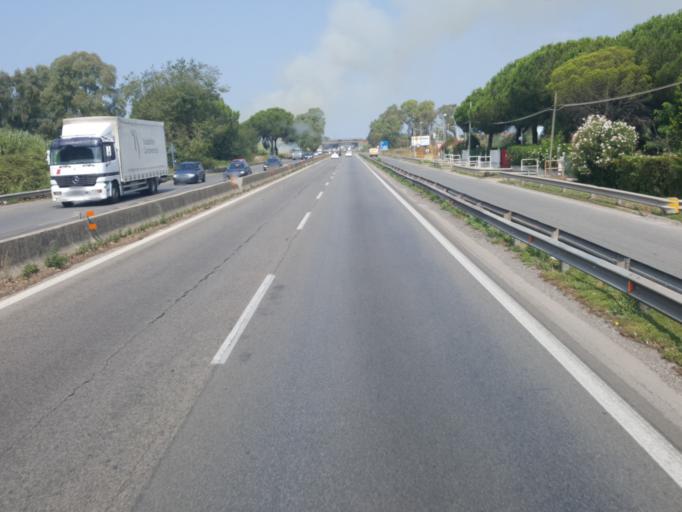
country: IT
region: Latium
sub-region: Provincia di Latina
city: Genio Civile
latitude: 41.5661
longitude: 12.6742
